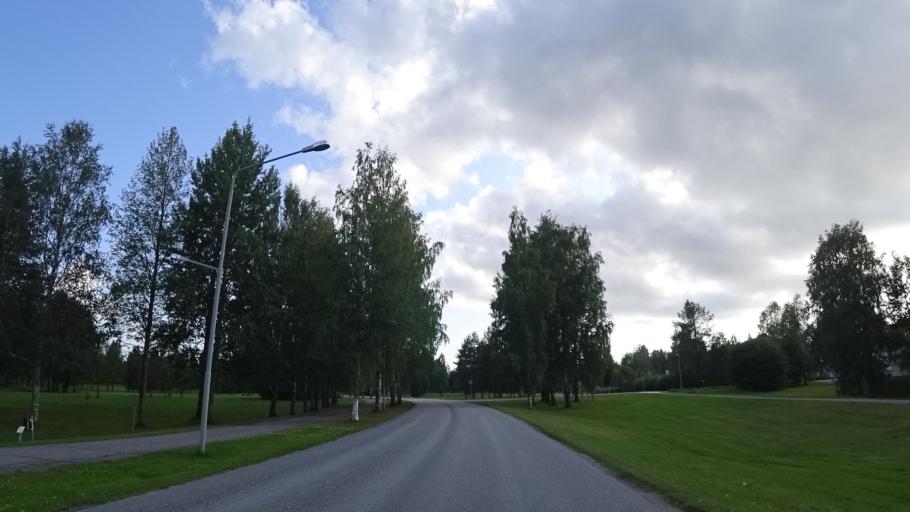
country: FI
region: North Karelia
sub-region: Pielisen Karjala
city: Lieksa
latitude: 63.3290
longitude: 30.0236
